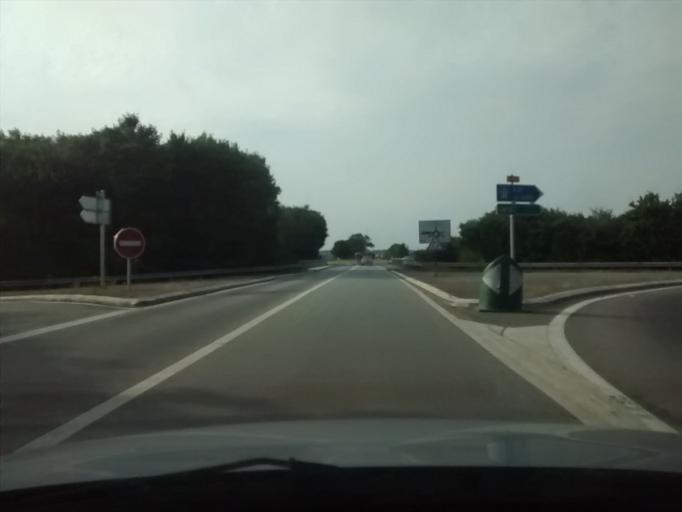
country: FR
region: Brittany
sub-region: Departement d'Ille-et-Vilaine
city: Etrelles
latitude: 48.0708
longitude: -1.1987
